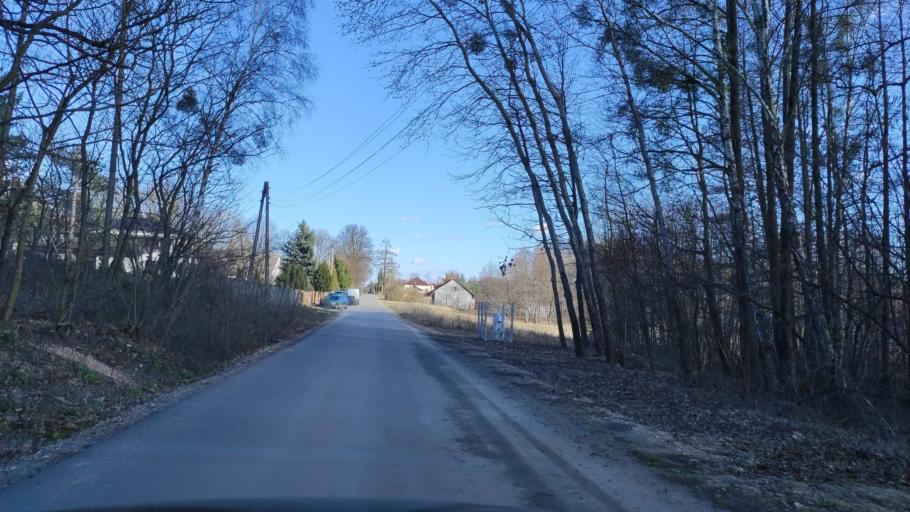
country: PL
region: Masovian Voivodeship
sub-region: Powiat radomski
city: Jedlnia-Letnisko
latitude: 51.4401
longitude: 21.2949
